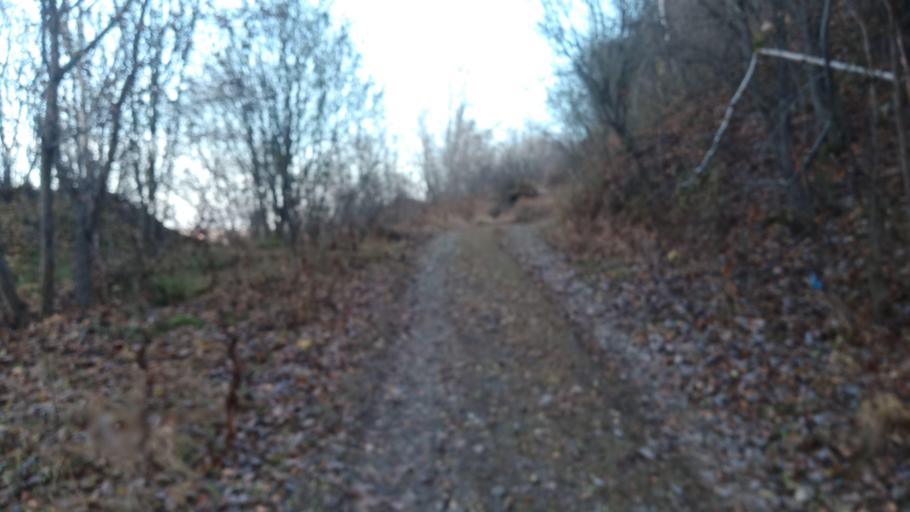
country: RU
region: Altai Krai
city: Gon'ba
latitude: 53.4344
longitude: 83.5513
